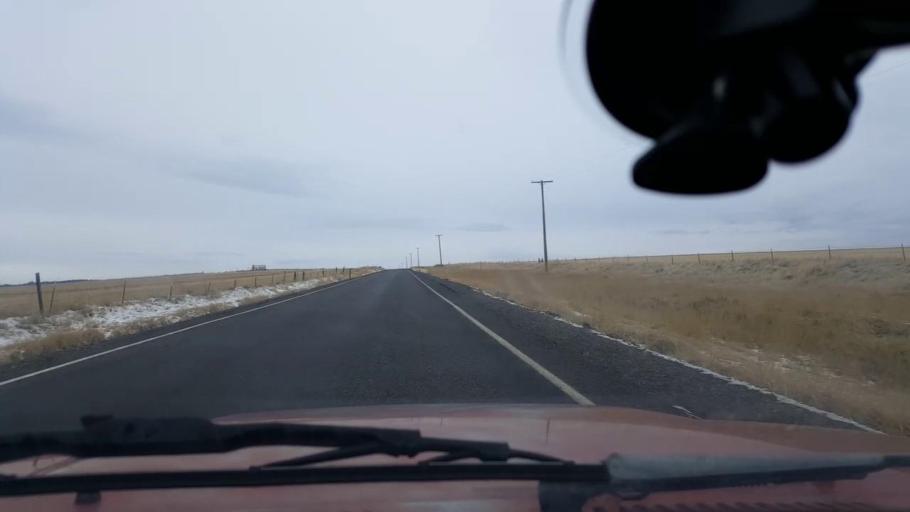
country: US
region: Washington
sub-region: Garfield County
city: Pomeroy
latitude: 46.3224
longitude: -117.3732
